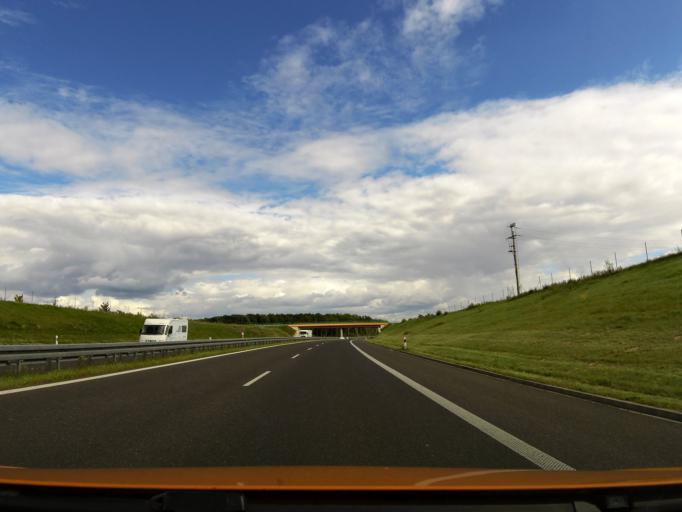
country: PL
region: West Pomeranian Voivodeship
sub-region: Powiat goleniowski
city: Nowogard
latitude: 53.6949
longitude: 15.1138
